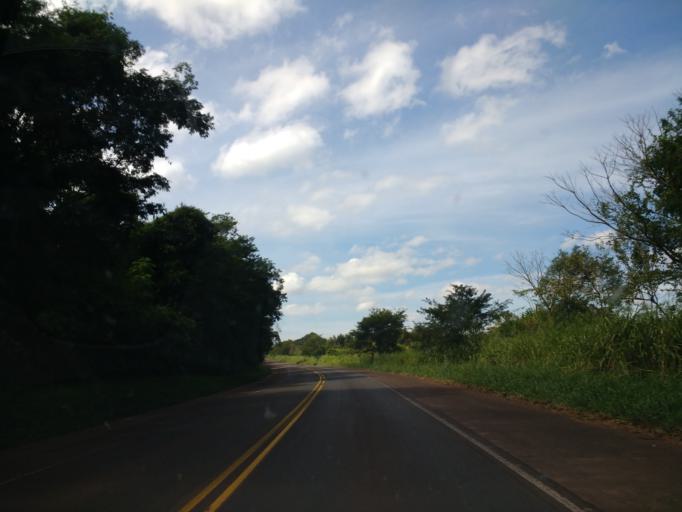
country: BR
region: Parana
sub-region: Terra Boa
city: Terra Boa
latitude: -23.6041
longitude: -52.3449
